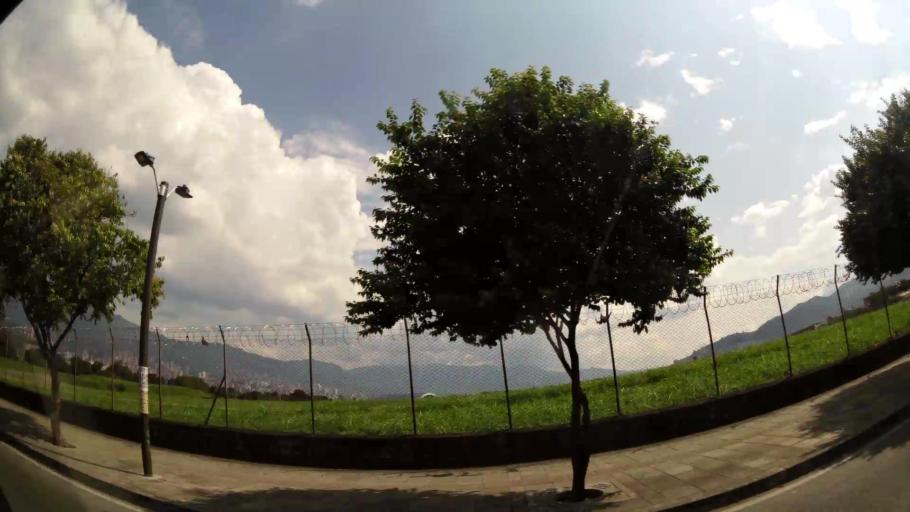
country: CO
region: Antioquia
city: San Vicente
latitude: 6.2393
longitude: -75.3415
